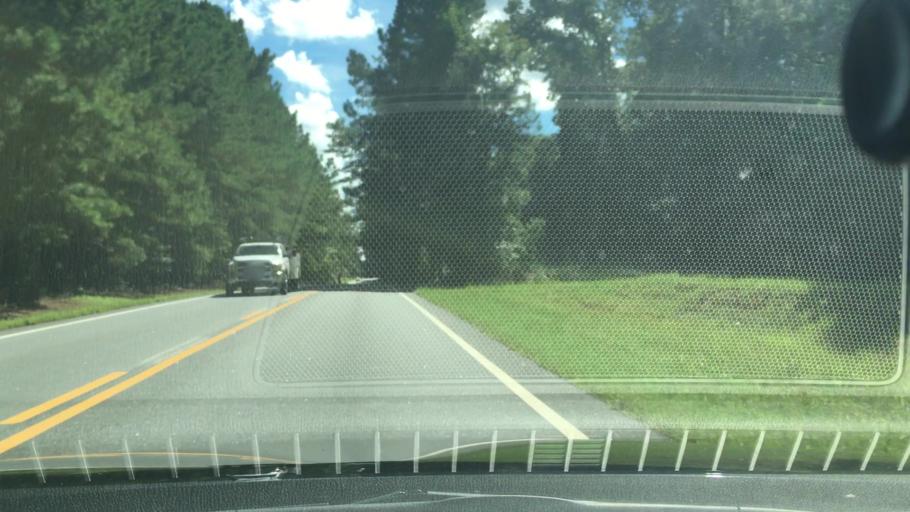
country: US
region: Georgia
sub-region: Butts County
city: Indian Springs
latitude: 33.2941
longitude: -83.8720
